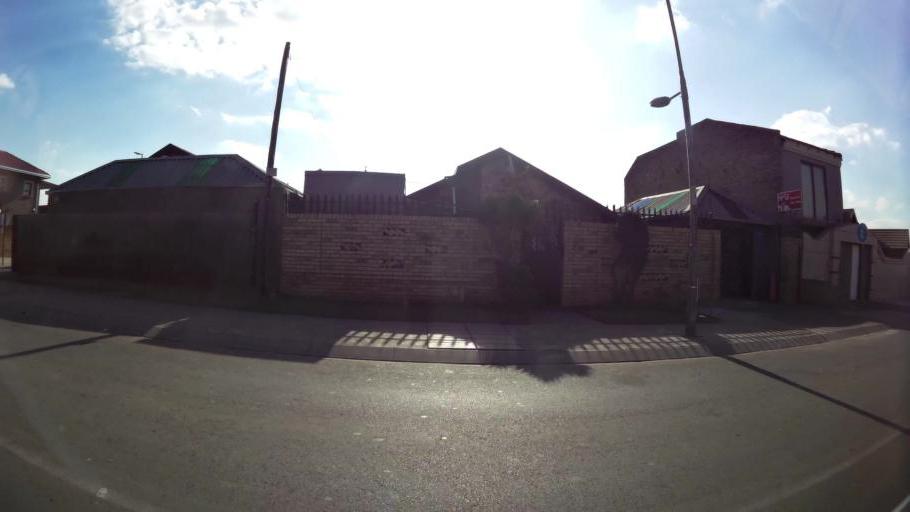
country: ZA
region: Gauteng
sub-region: City of Johannesburg Metropolitan Municipality
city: Soweto
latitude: -26.2529
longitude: 27.9106
